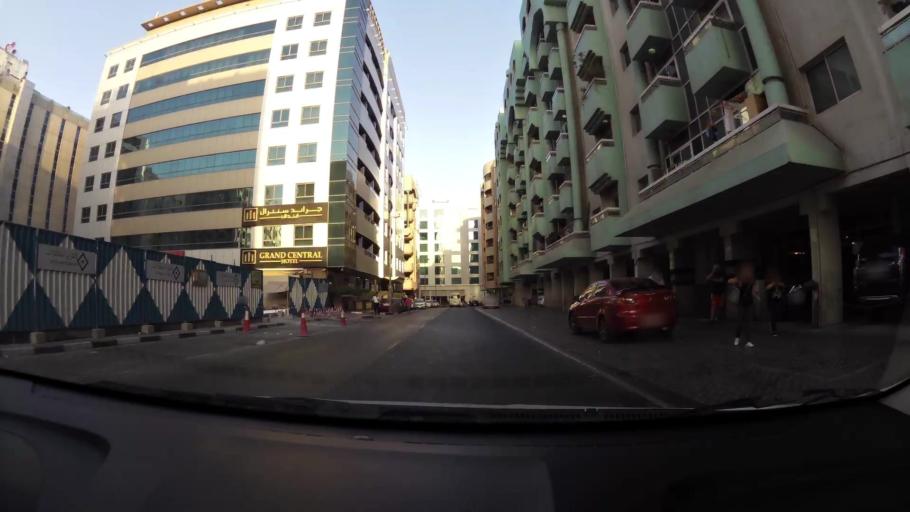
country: AE
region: Ash Shariqah
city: Sharjah
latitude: 25.2639
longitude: 55.3263
